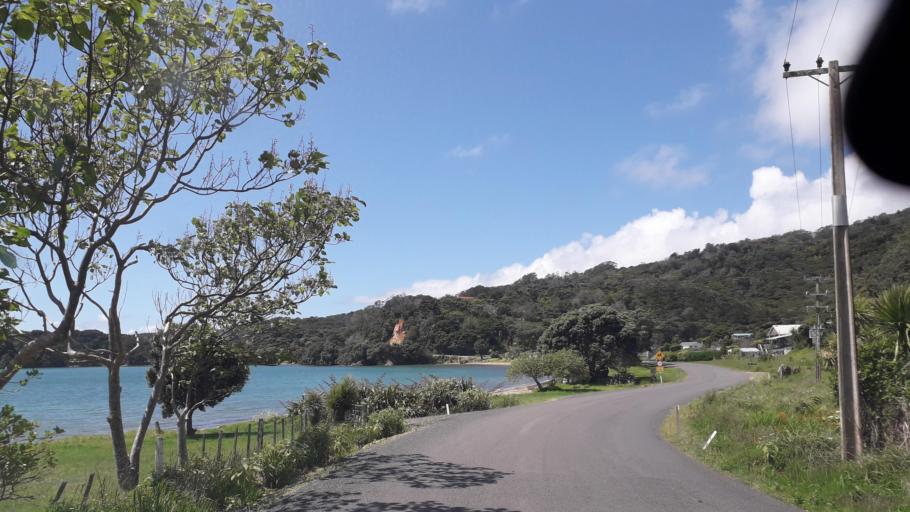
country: NZ
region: Northland
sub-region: Far North District
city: Paihia
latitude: -35.2378
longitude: 174.2578
